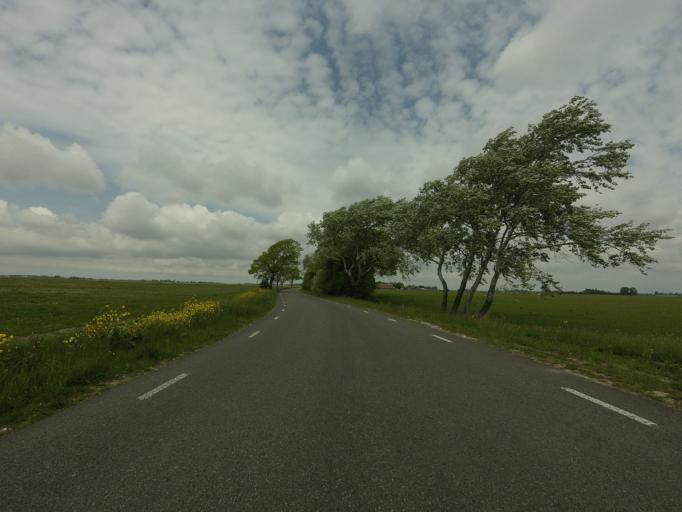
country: NL
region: Friesland
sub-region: Sudwest Fryslan
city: Bolsward
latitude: 53.0941
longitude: 5.5344
